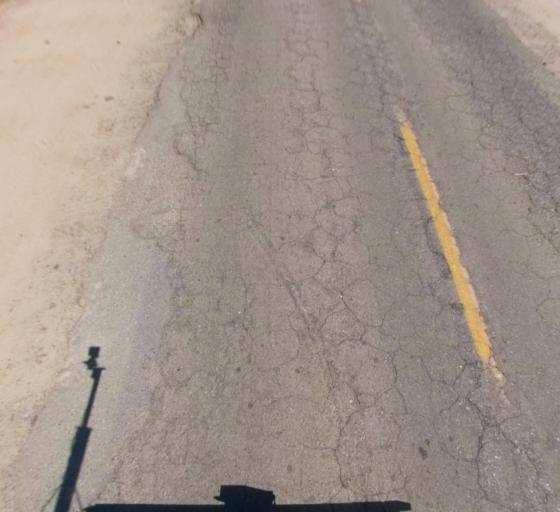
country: US
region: California
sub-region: Fresno County
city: Biola
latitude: 36.8615
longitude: -120.0194
